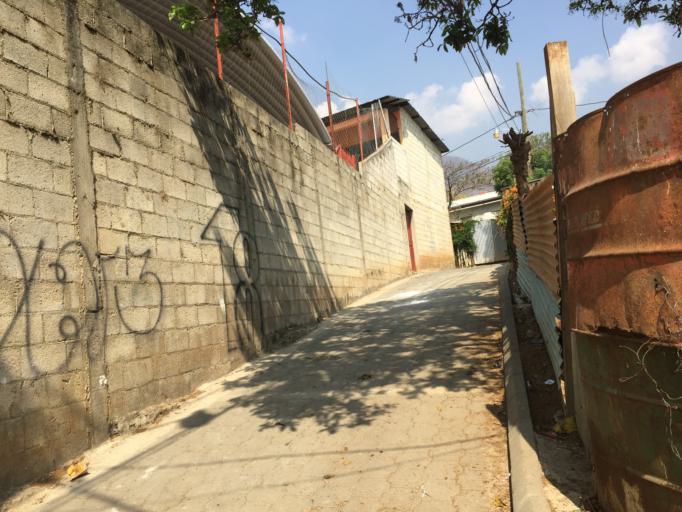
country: GT
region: Guatemala
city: Amatitlan
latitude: 14.4981
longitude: -90.6443
